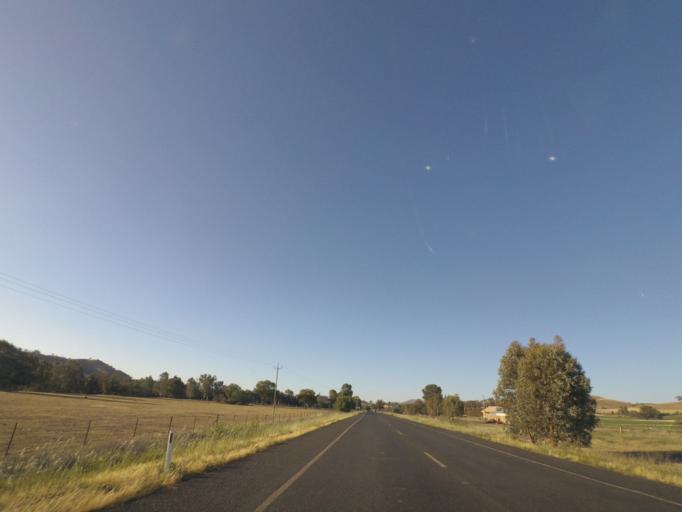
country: AU
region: New South Wales
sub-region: Gundagai
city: Gundagai
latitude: -34.9346
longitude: 148.1671
